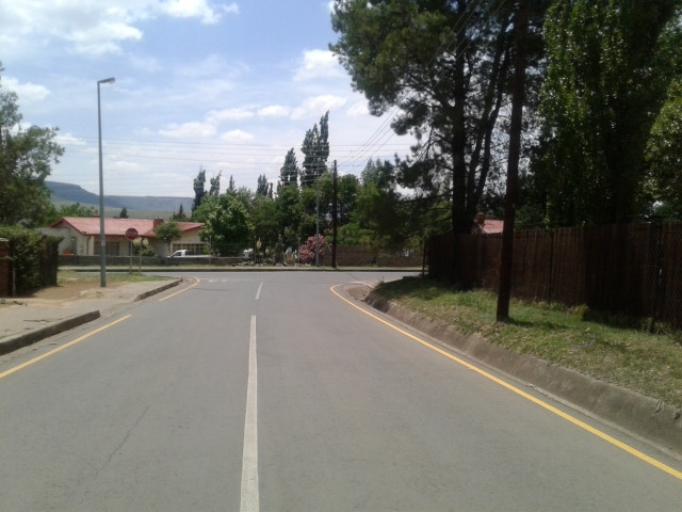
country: LS
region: Maseru
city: Maseru
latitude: -29.3032
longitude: 27.4718
